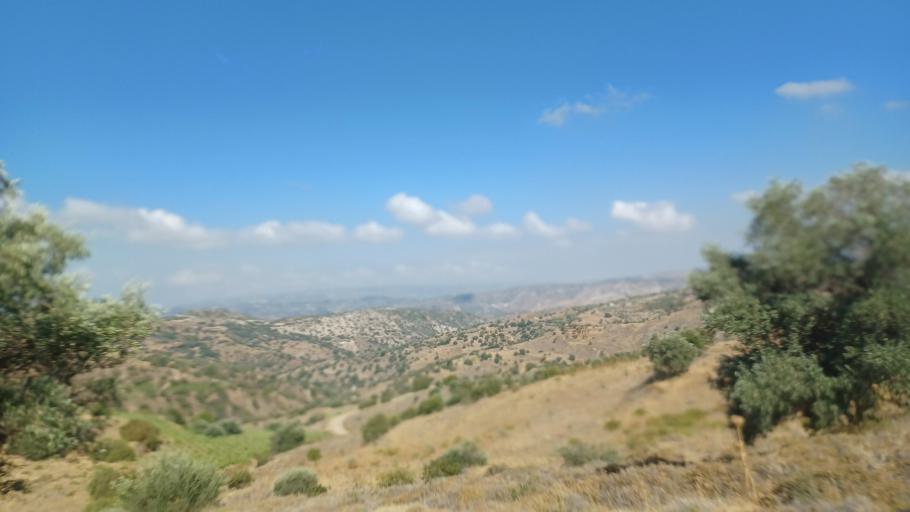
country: CY
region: Pafos
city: Mesogi
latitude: 34.8765
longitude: 32.5987
